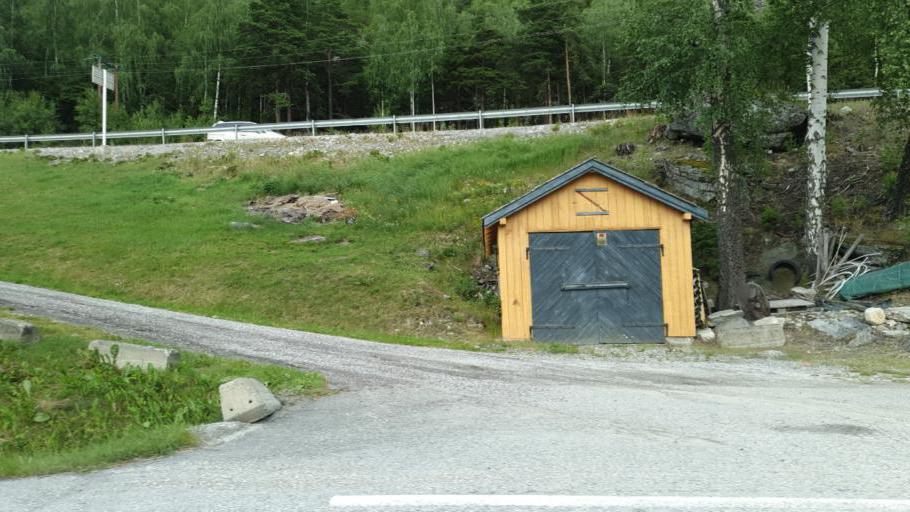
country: NO
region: Oppland
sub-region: Sel
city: Otta
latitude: 61.8488
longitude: 9.4304
